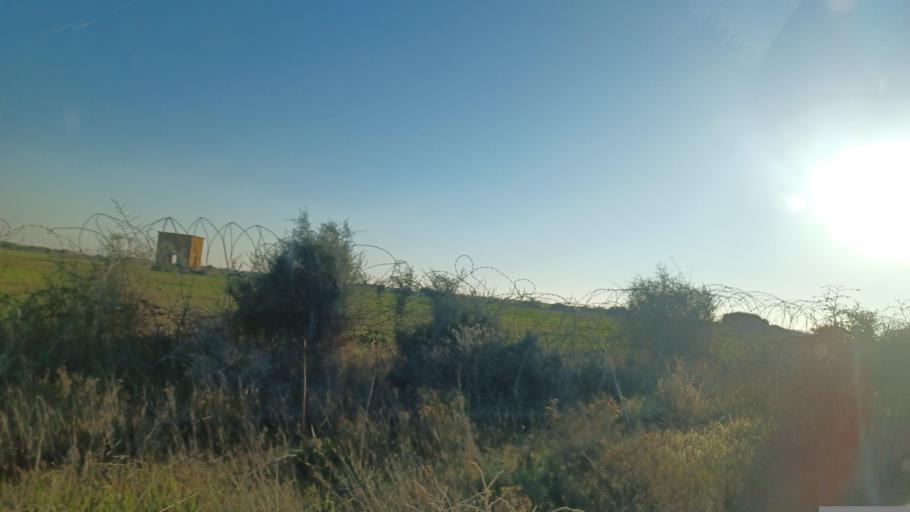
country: CY
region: Lefkosia
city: Kato Deftera
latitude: 35.1407
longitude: 33.2755
